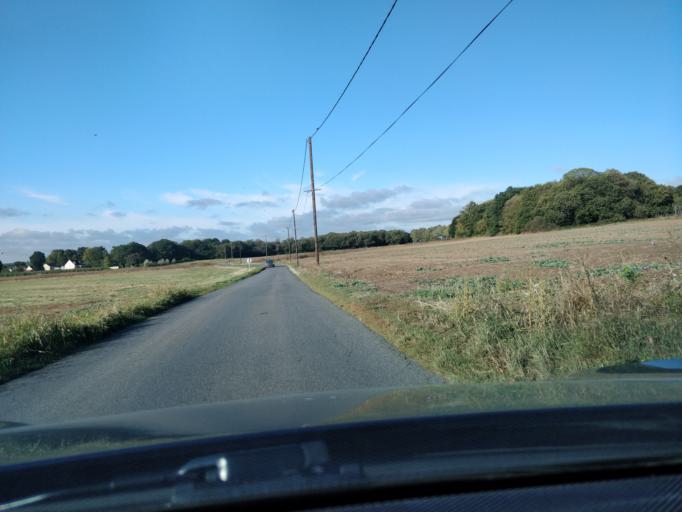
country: FR
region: Ile-de-France
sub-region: Departement de l'Essonne
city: Vaugrigneuse
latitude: 48.6081
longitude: 2.1030
